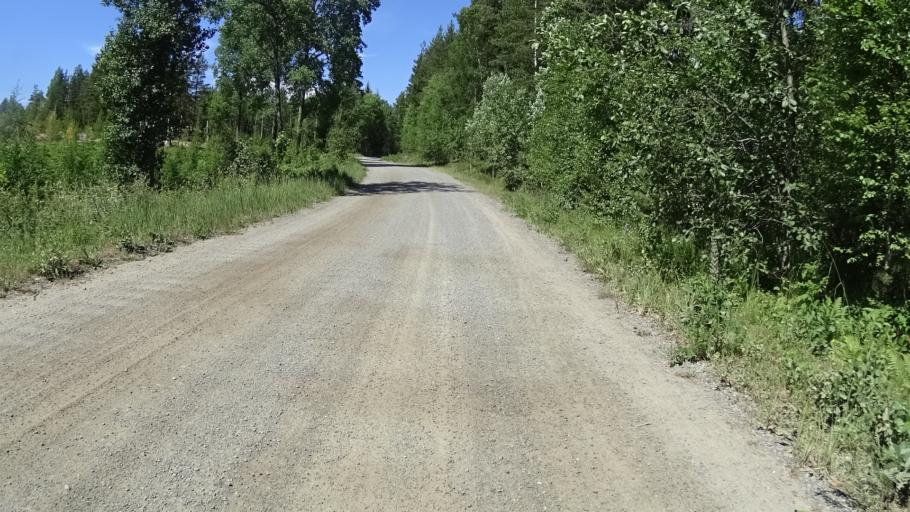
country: FI
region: Uusimaa
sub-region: Raaseporin
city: Pohja
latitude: 60.0960
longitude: 23.5632
